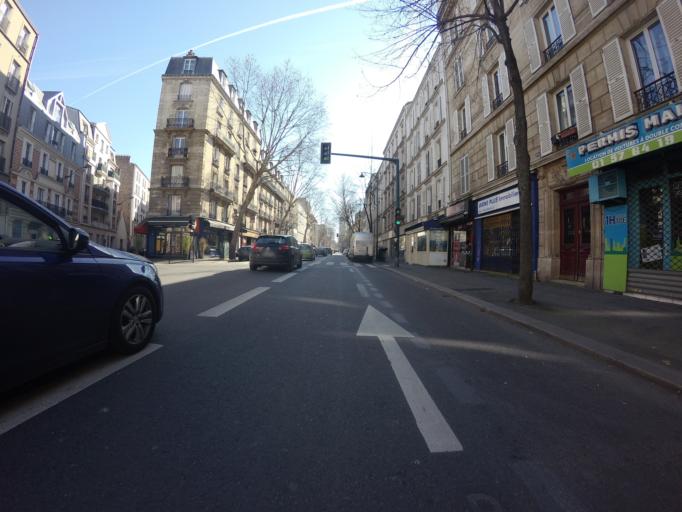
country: FR
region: Ile-de-France
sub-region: Departement des Hauts-de-Seine
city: Clichy
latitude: 48.9053
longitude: 2.3019
